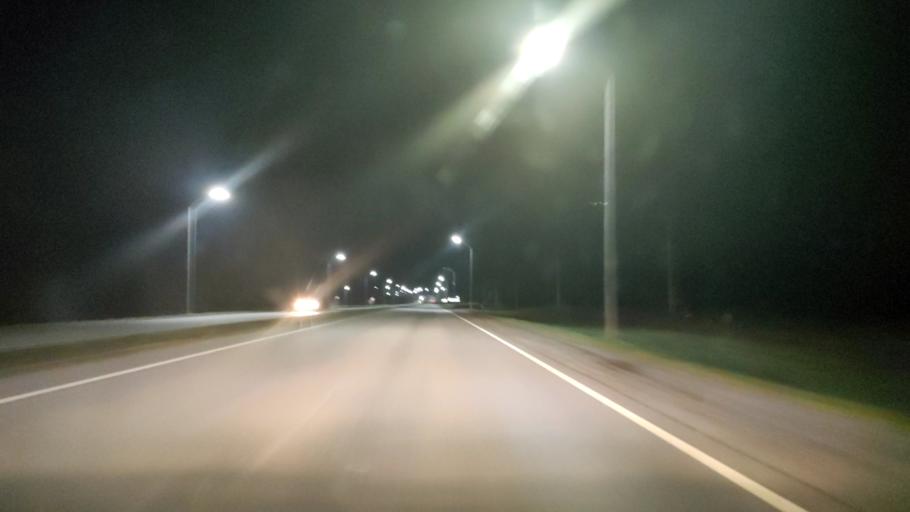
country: RU
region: Belgorod
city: Staryy Oskol
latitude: 51.3873
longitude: 37.8624
